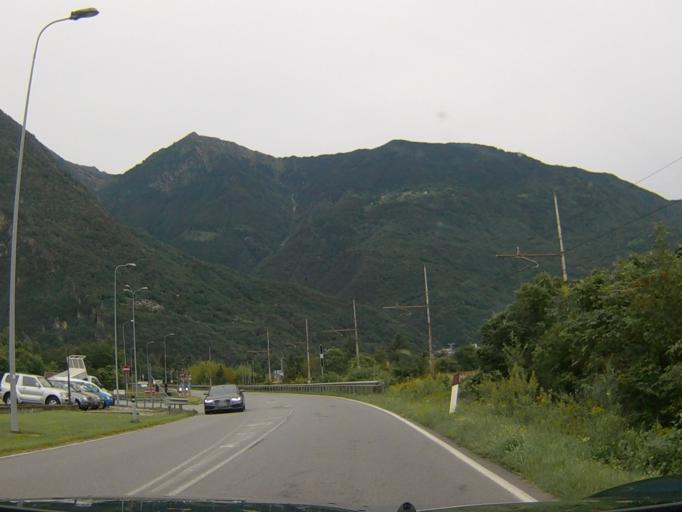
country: IT
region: Lombardy
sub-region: Provincia di Sondrio
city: Novate Mezzola
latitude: 46.2119
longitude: 9.4487
